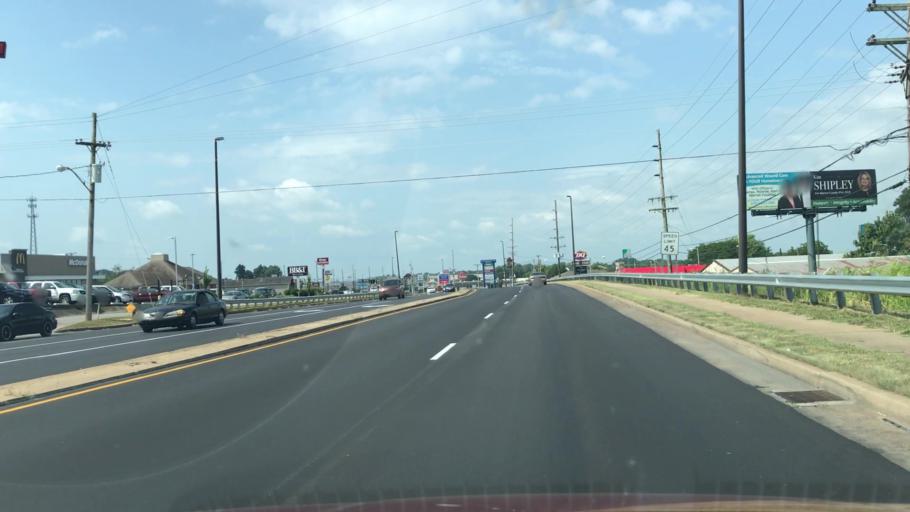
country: US
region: Kentucky
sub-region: Barren County
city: Glasgow
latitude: 37.0092
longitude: -85.9221
